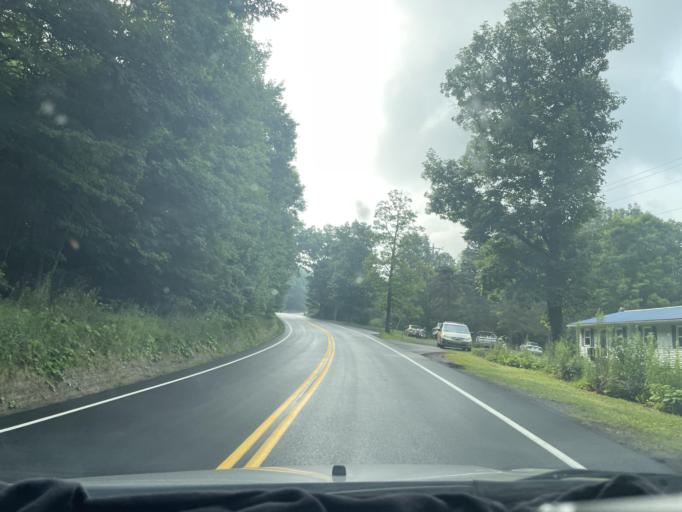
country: US
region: Maryland
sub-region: Garrett County
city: Mountain Lake Park
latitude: 39.3020
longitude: -79.3953
